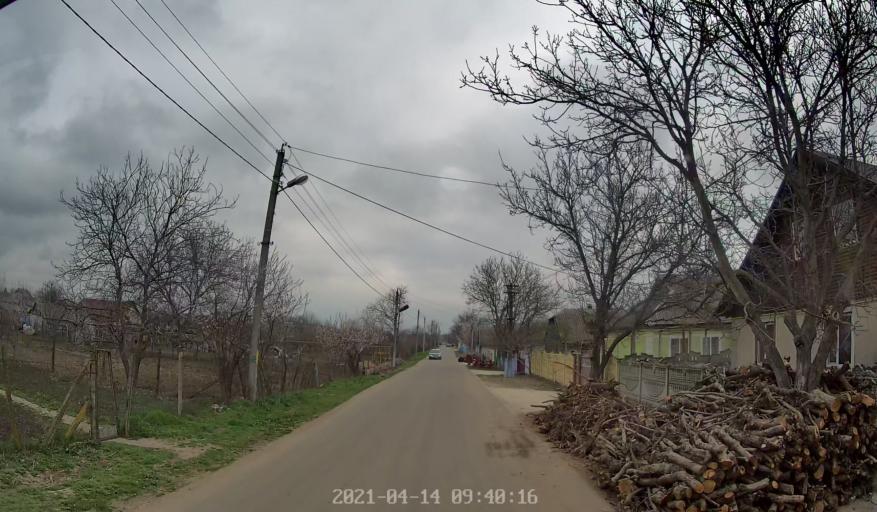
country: MD
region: Chisinau
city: Vadul lui Voda
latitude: 47.1344
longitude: 29.1257
